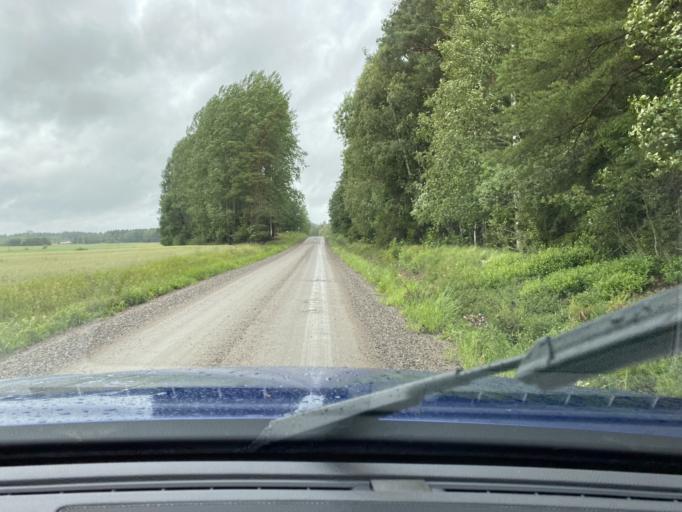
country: FI
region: Pirkanmaa
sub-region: Lounais-Pirkanmaa
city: Punkalaidun
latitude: 61.1490
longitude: 23.2365
